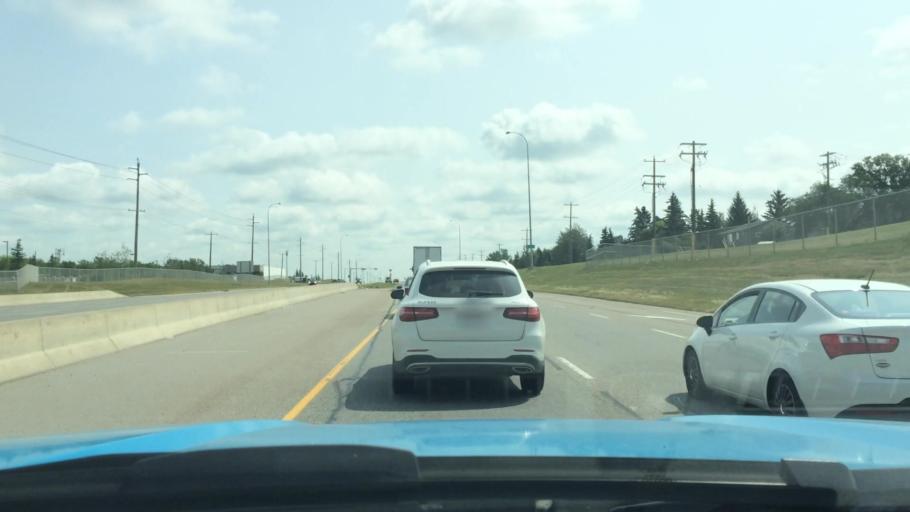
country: CA
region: Alberta
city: Calgary
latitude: 51.0960
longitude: -113.9713
